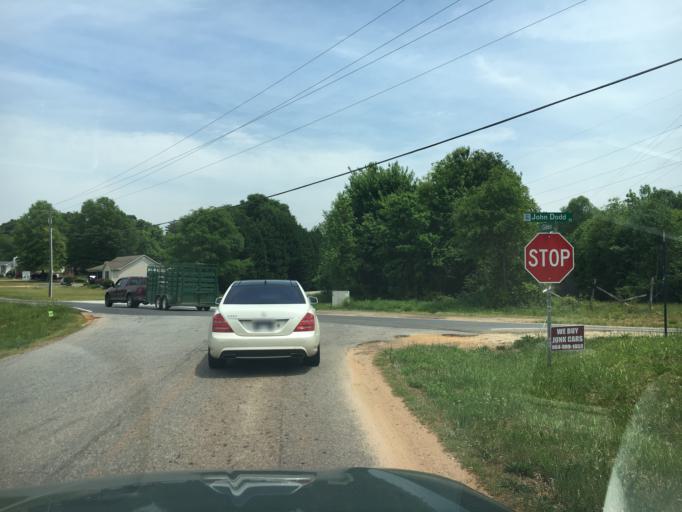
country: US
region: South Carolina
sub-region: Spartanburg County
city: Wellford
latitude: 34.9862
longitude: -82.0777
